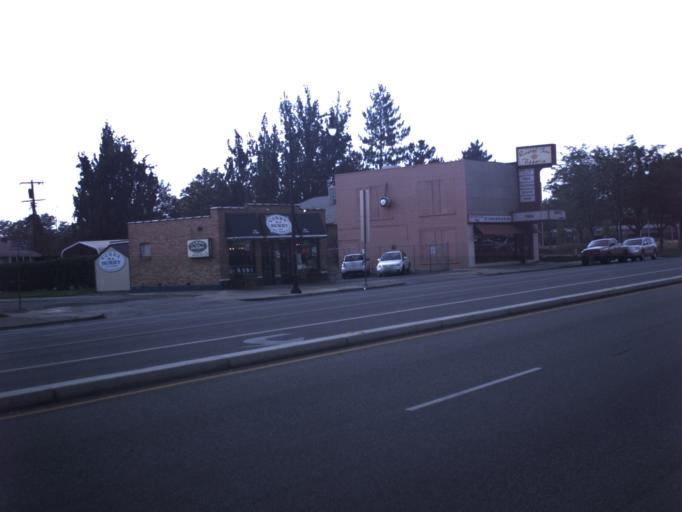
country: US
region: Utah
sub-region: Salt Lake County
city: South Salt Lake
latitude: 40.7258
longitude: -111.8881
